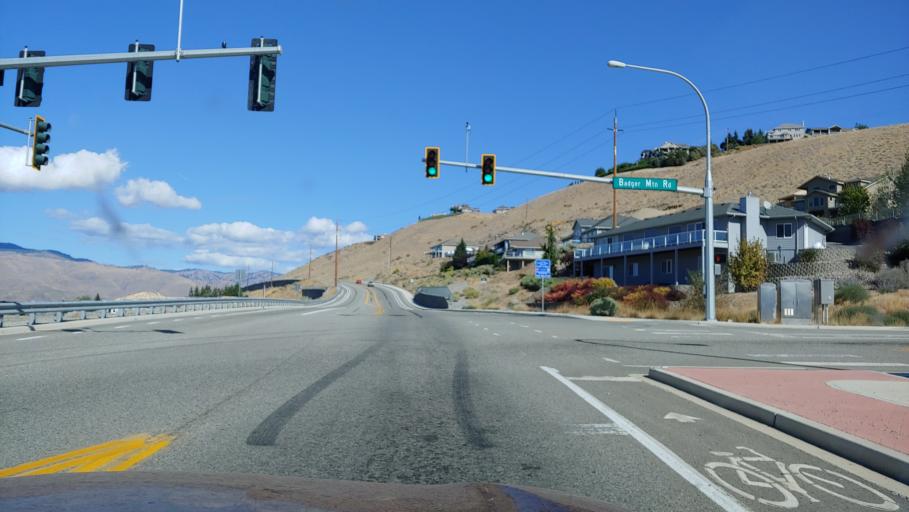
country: US
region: Washington
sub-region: Douglas County
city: East Wenatchee Bench
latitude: 47.4392
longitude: -120.2829
